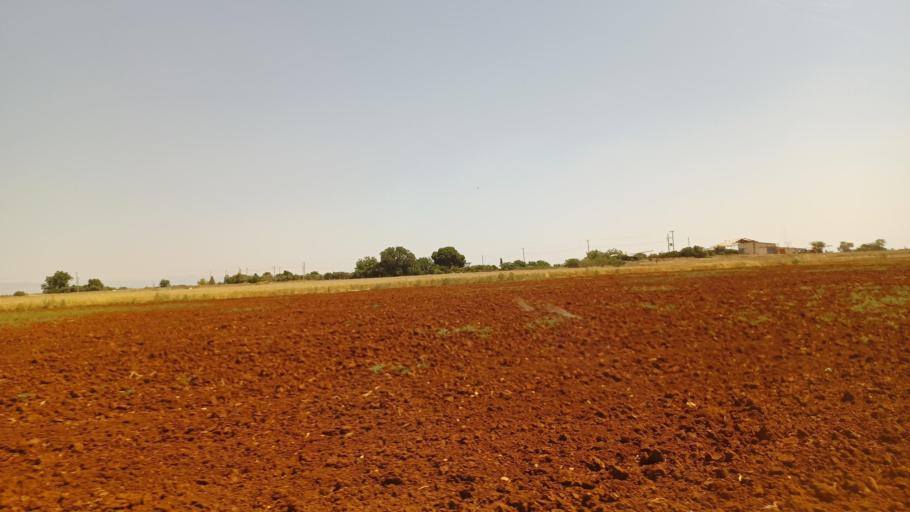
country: CY
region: Ammochostos
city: Avgorou
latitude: 35.0280
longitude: 33.8115
